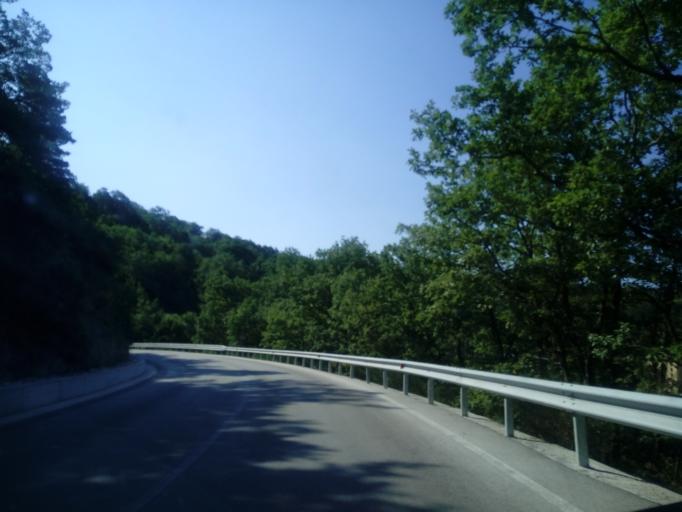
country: IT
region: Molise
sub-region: Provincia di Campobasso
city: Gildone
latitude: 41.5103
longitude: 14.7428
